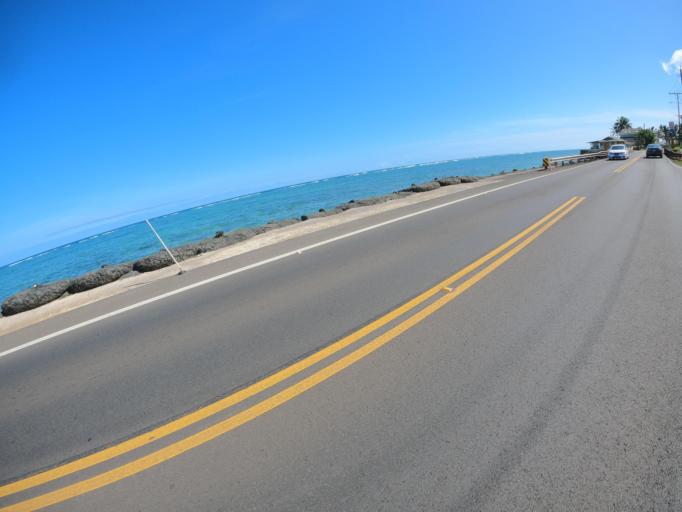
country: US
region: Hawaii
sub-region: Honolulu County
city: Hau'ula
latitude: 21.6036
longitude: -157.8996
